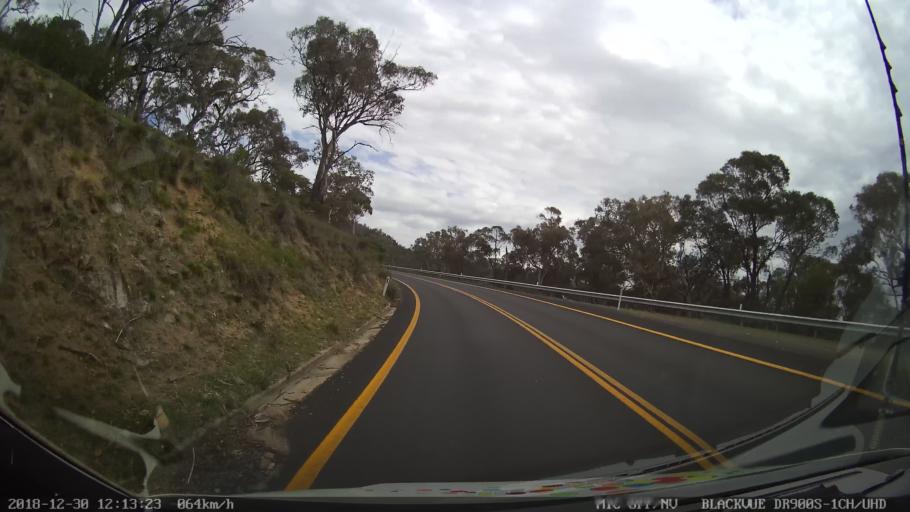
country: AU
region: New South Wales
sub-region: Snowy River
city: Jindabyne
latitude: -36.3491
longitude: 148.5855
